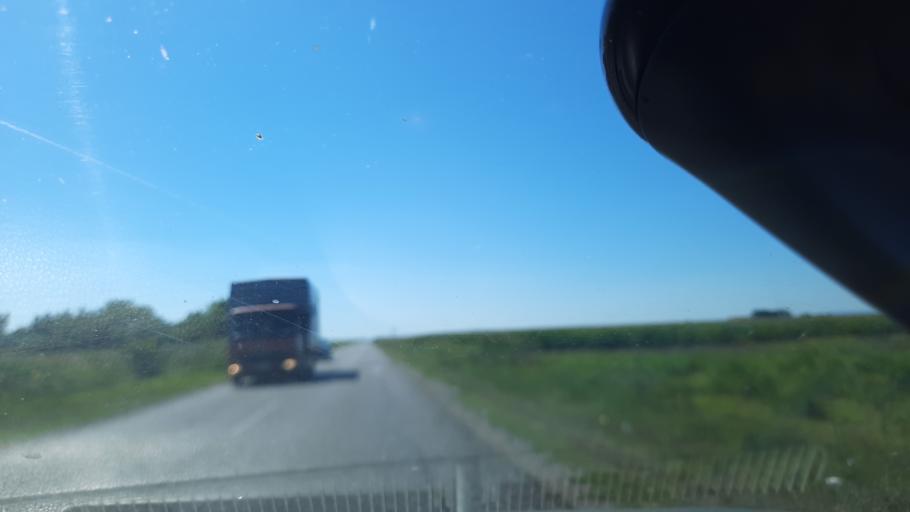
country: RS
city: Simanovci
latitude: 44.8783
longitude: 20.0634
